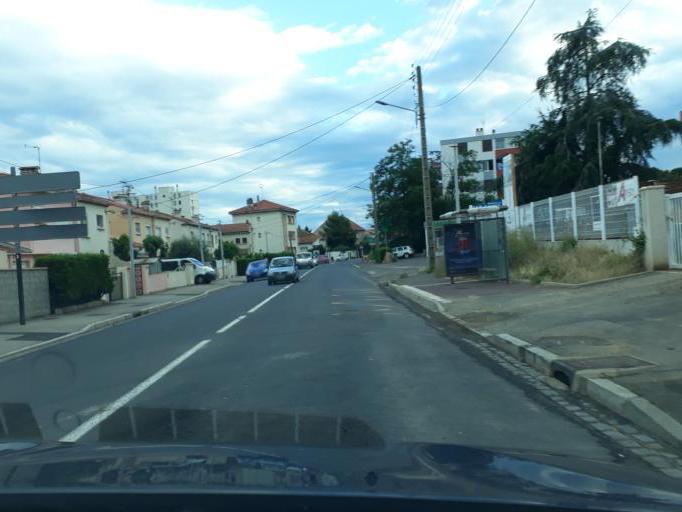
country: FR
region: Languedoc-Roussillon
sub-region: Departement de l'Herault
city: Beziers
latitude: 43.3371
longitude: 3.2362
